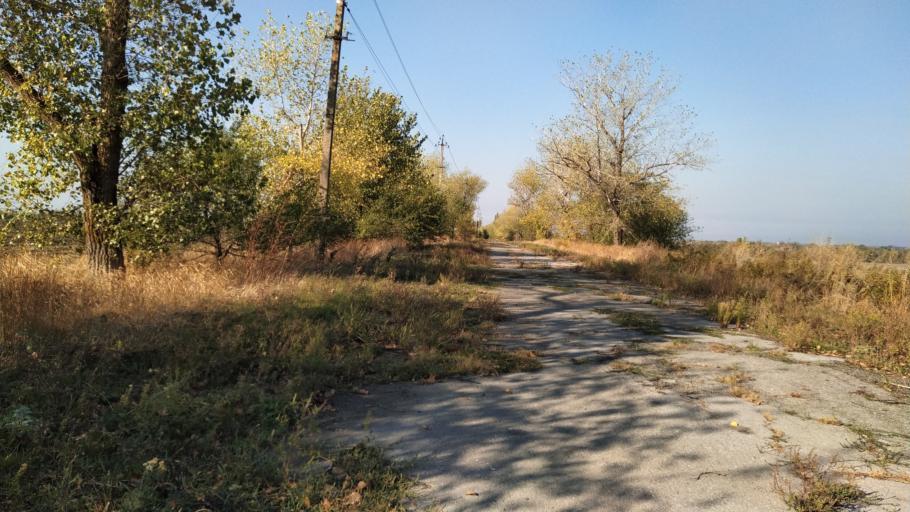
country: RU
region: Rostov
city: Bataysk
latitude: 47.0891
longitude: 39.7763
